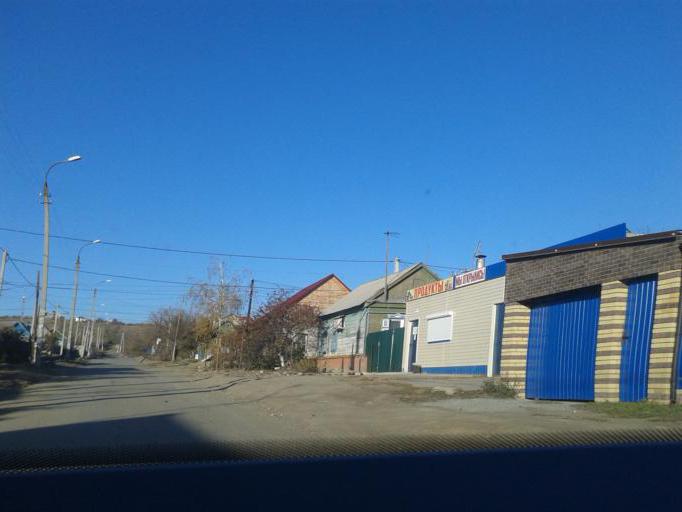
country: RU
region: Volgograd
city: Volgograd
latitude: 48.6110
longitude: 44.4154
